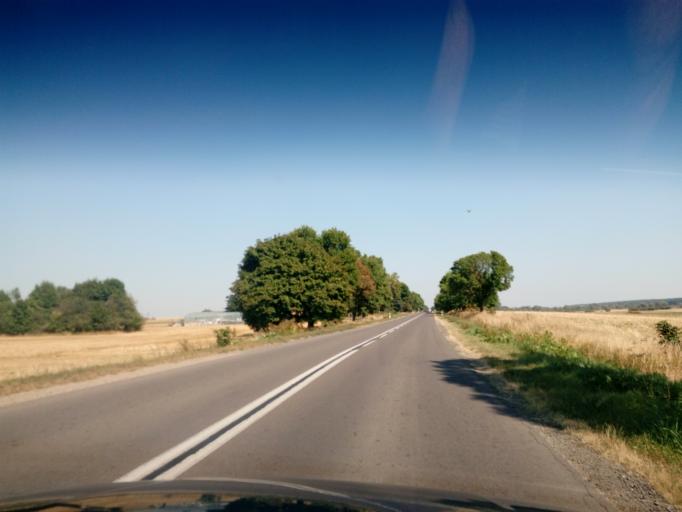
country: PL
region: Lublin Voivodeship
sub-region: Powiat hrubieszowski
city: Hrubieszow
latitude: 50.8301
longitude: 23.9595
